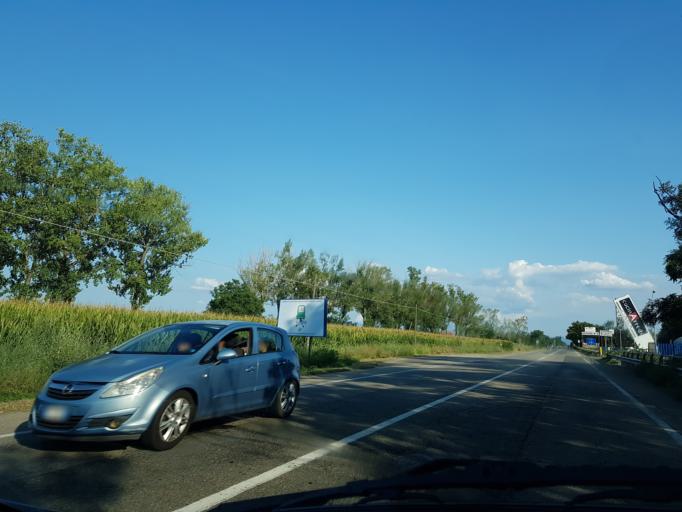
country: IT
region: Piedmont
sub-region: Provincia di Alessandria
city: Litta Parodi-Cascinagrossa
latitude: 44.8549
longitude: 8.7149
